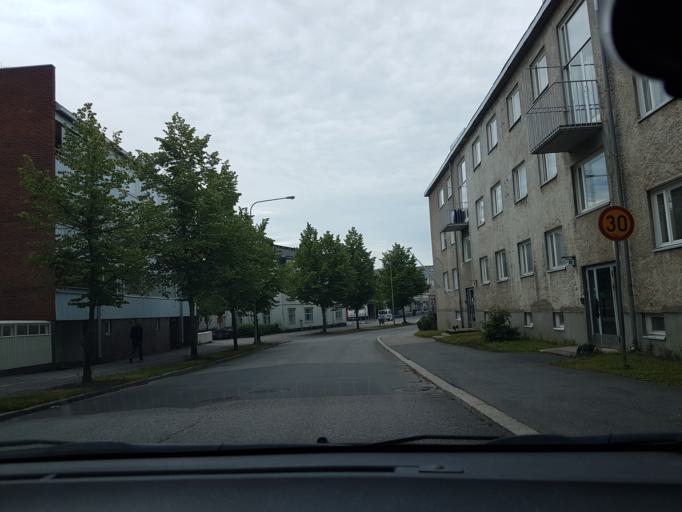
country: FI
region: Uusimaa
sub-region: Helsinki
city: Vantaa
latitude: 60.2534
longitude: 25.0085
